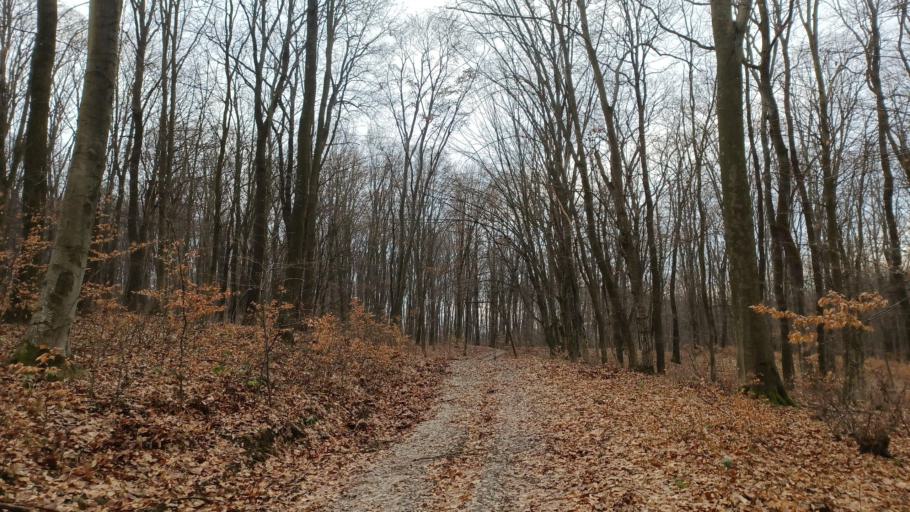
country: HU
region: Tolna
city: Szentgalpuszta
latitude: 46.3141
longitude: 18.6467
